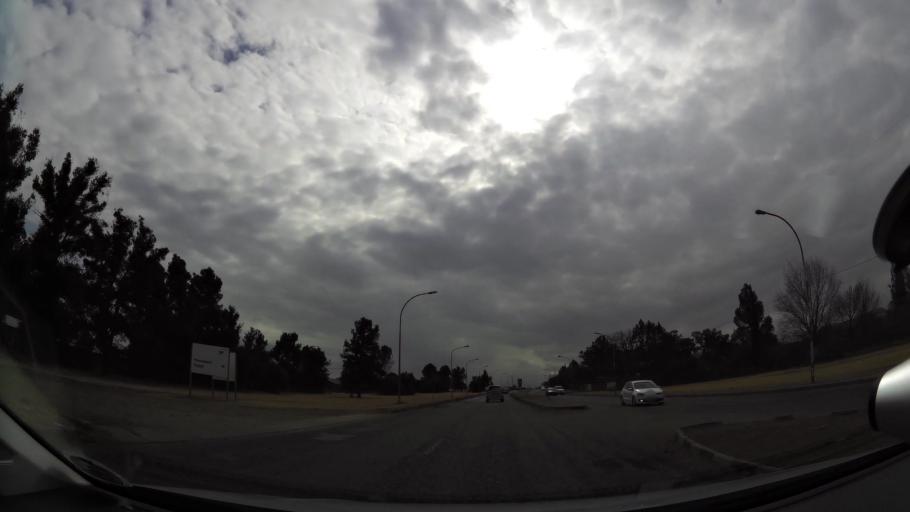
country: ZA
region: Orange Free State
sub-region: Fezile Dabi District Municipality
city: Kroonstad
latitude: -27.6567
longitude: 27.2303
